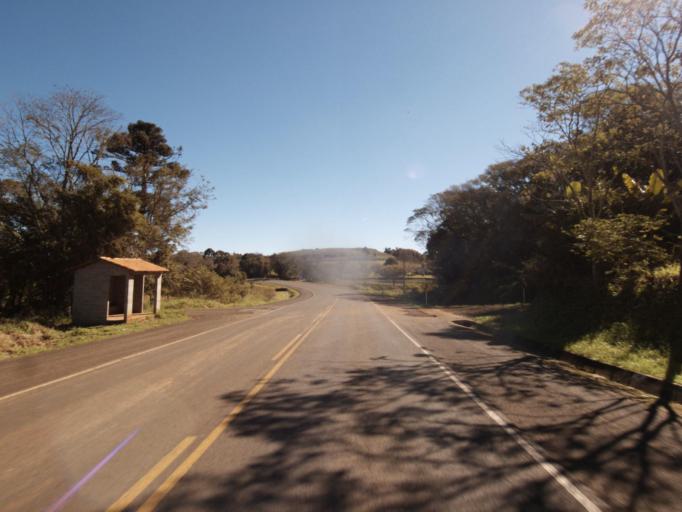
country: AR
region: Misiones
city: Bernardo de Irigoyen
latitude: -26.6699
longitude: -53.5748
